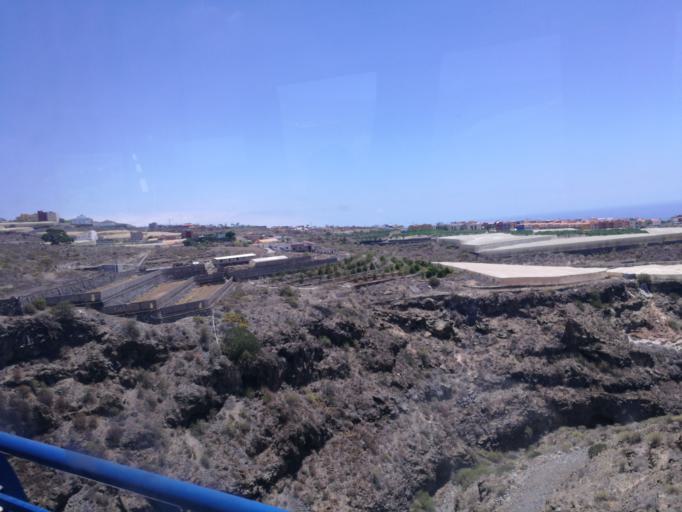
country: ES
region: Canary Islands
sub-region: Provincia de Santa Cruz de Tenerife
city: Guia de Isora
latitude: 28.1866
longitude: -16.7900
